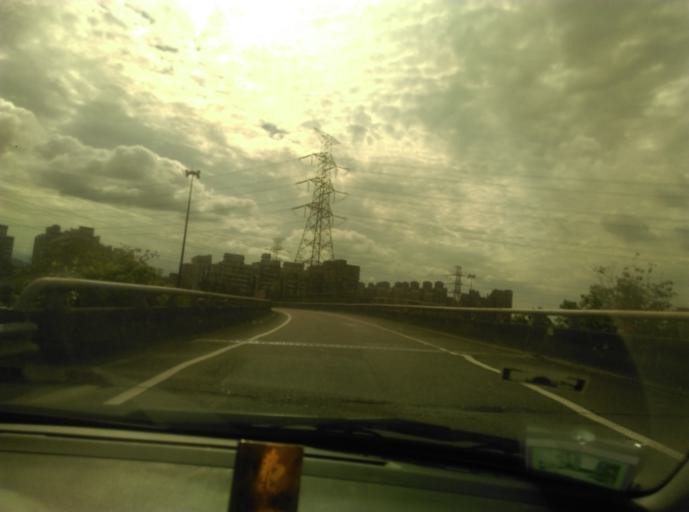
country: TW
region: Taiwan
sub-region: Keelung
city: Keelung
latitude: 25.0731
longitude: 121.6443
